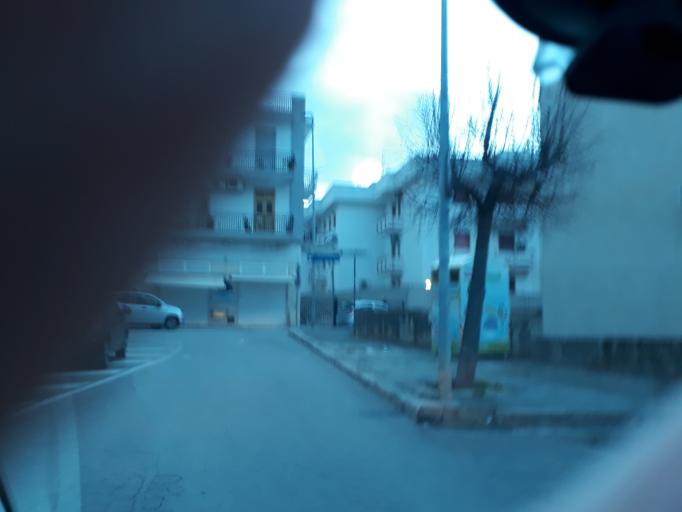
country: IT
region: Apulia
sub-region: Provincia di Brindisi
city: Fasano
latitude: 40.8360
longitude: 17.3534
